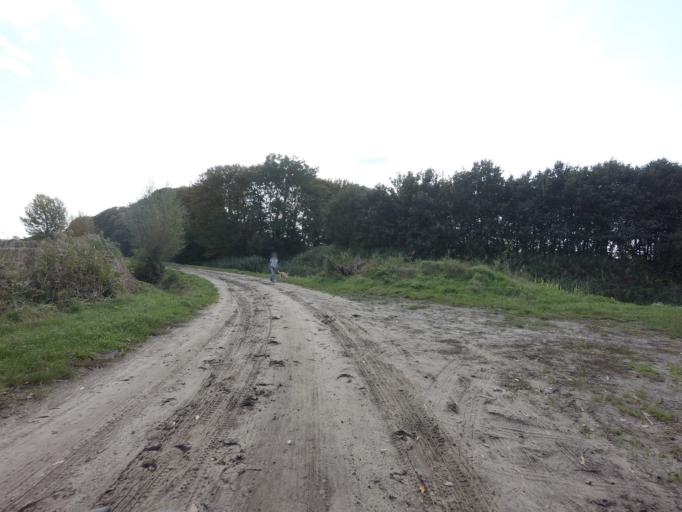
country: NL
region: North Brabant
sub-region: Gemeente Breda
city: Hoge Vucht
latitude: 51.6195
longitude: 4.7755
